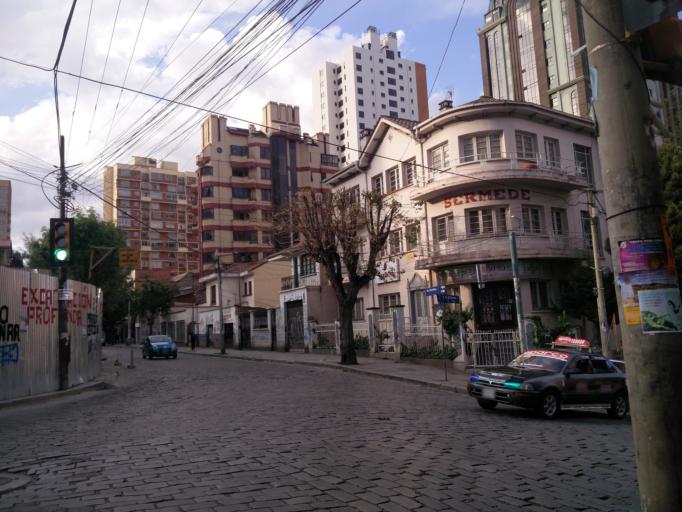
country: BO
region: La Paz
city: La Paz
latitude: -16.5106
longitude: -68.1291
